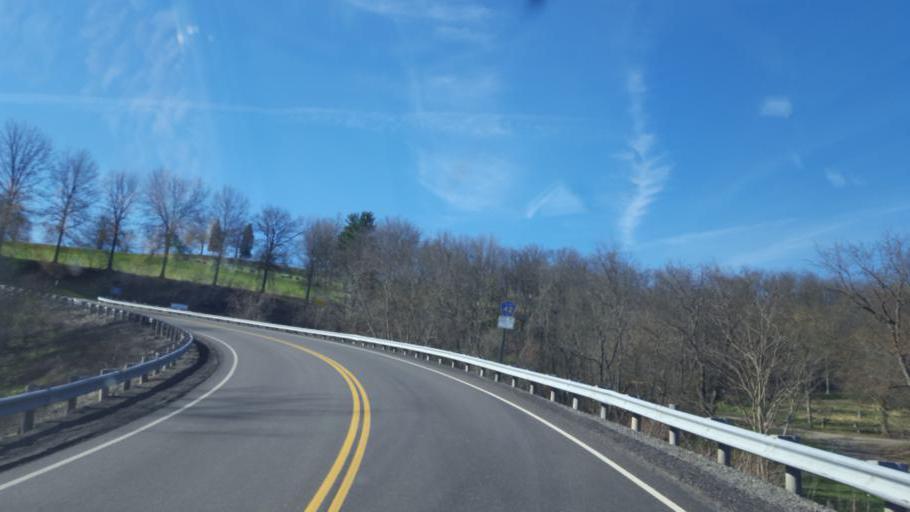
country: US
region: Ohio
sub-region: Jefferson County
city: Toronto
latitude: 40.4657
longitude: -80.6117
